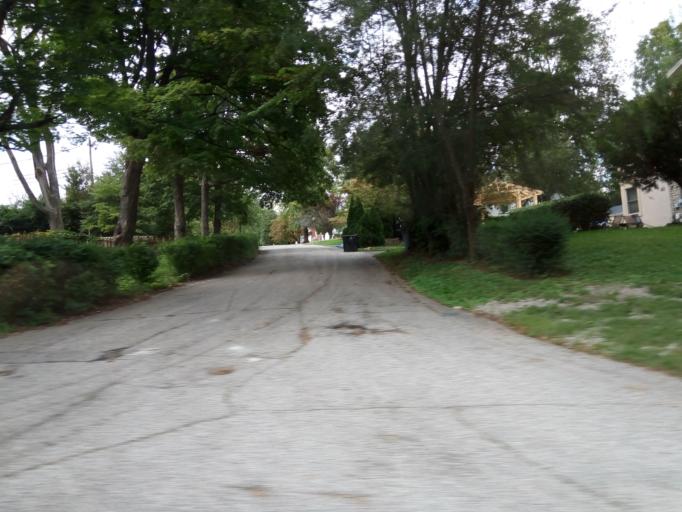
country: US
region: Kentucky
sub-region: Jefferson County
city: Audubon Park
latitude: 38.2090
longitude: -85.7201
